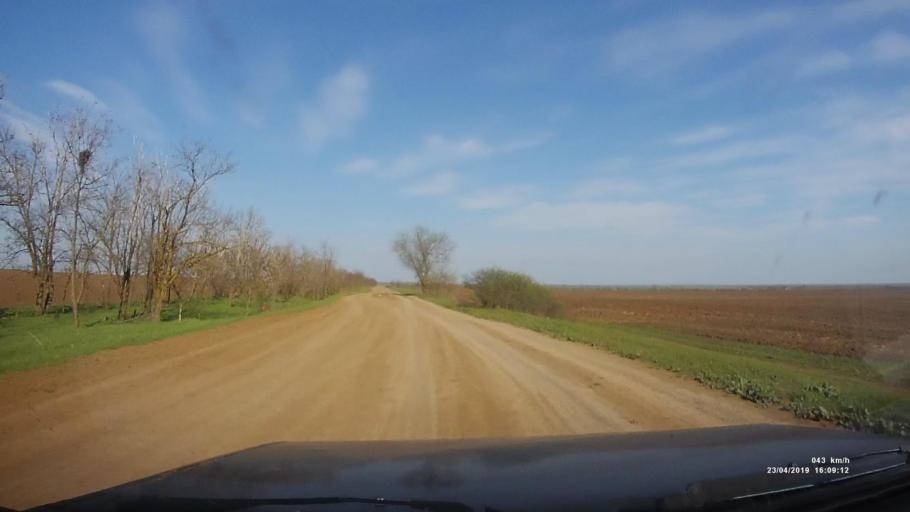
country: RU
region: Rostov
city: Remontnoye
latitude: 46.4816
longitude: 43.1087
